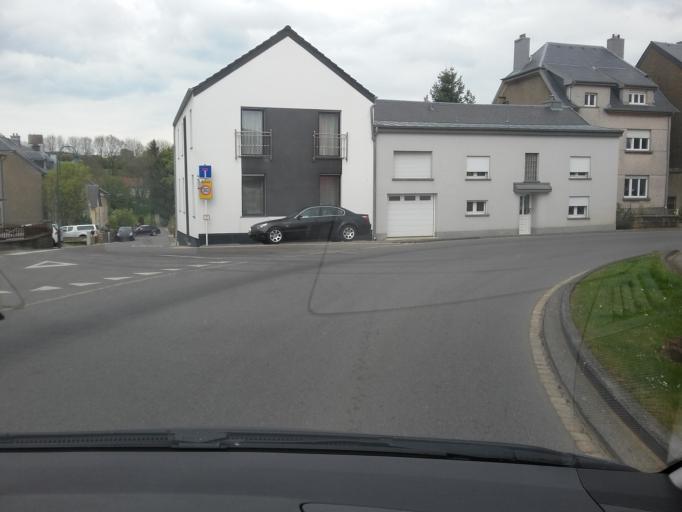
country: LU
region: Luxembourg
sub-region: Canton de Capellen
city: Clemency
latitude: 49.5966
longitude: 5.8755
